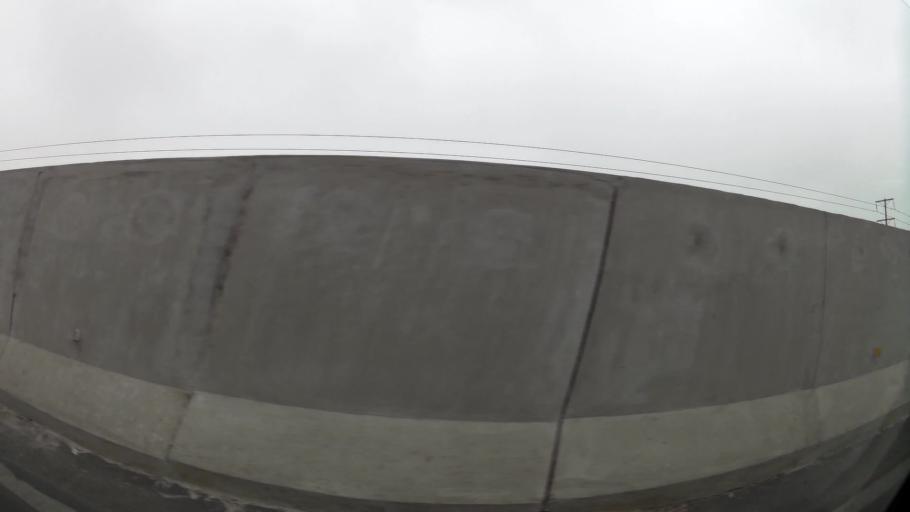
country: PE
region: Lima
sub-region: Lima
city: Urb. Santo Domingo
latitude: -11.9062
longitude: -77.0692
